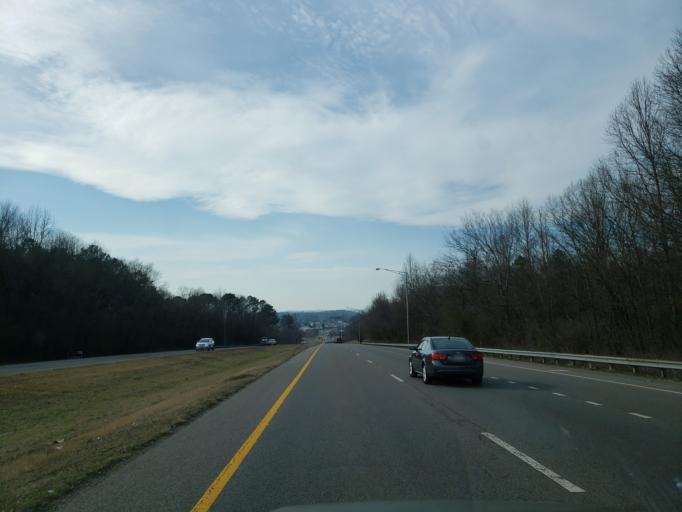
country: US
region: Tennessee
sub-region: Bradley County
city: East Cleveland
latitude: 35.1709
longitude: -84.8517
